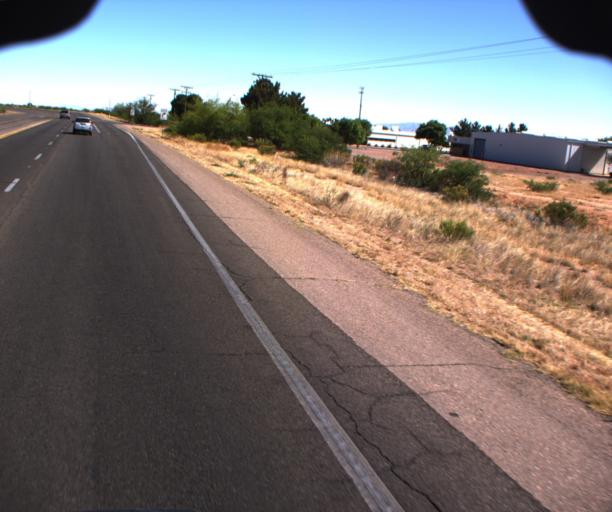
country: US
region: Arizona
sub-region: Cochise County
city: Sierra Vista
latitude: 31.5637
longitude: -110.2572
